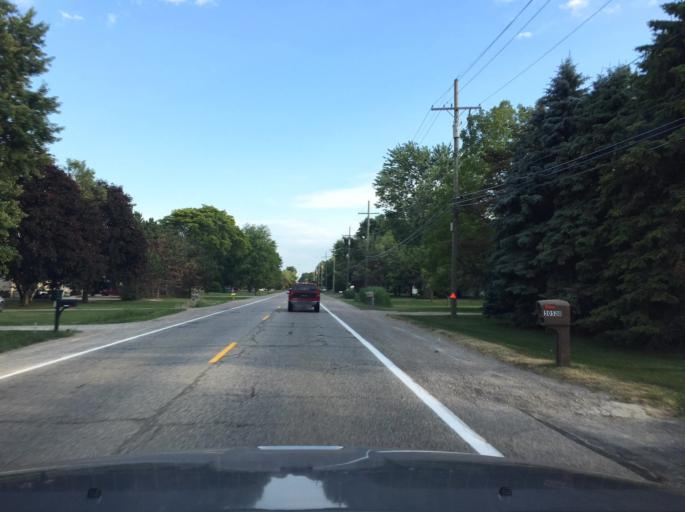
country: US
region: Michigan
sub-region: Macomb County
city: Mount Clemens
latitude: 42.6701
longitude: -82.8777
